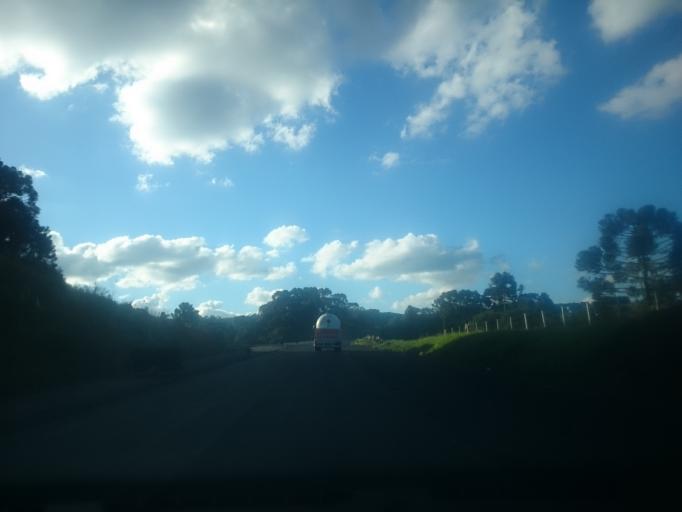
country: BR
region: Santa Catarina
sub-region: Sao Joaquim
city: Sao Joaquim
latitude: -28.0778
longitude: -50.0709
